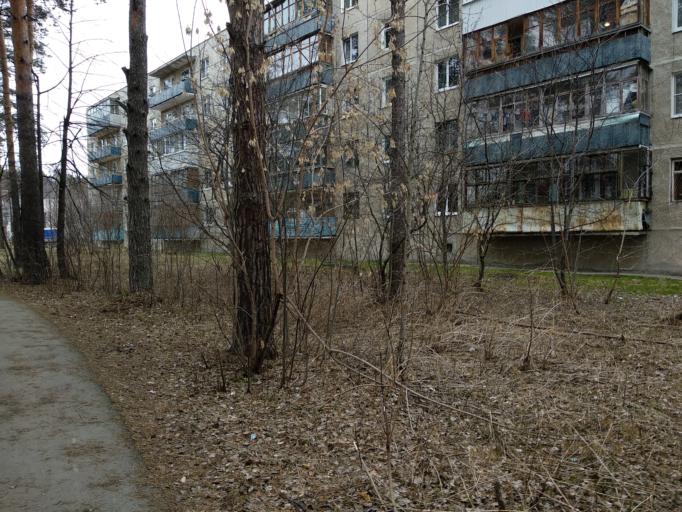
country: RU
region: Sverdlovsk
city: Beryozovsky
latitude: 56.9027
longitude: 60.7491
